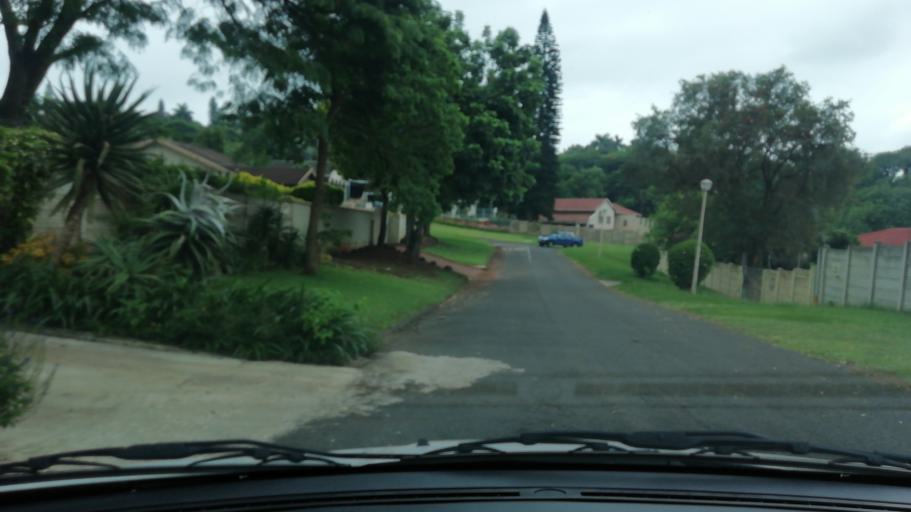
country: ZA
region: KwaZulu-Natal
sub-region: uThungulu District Municipality
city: Empangeni
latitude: -28.7585
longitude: 31.8889
